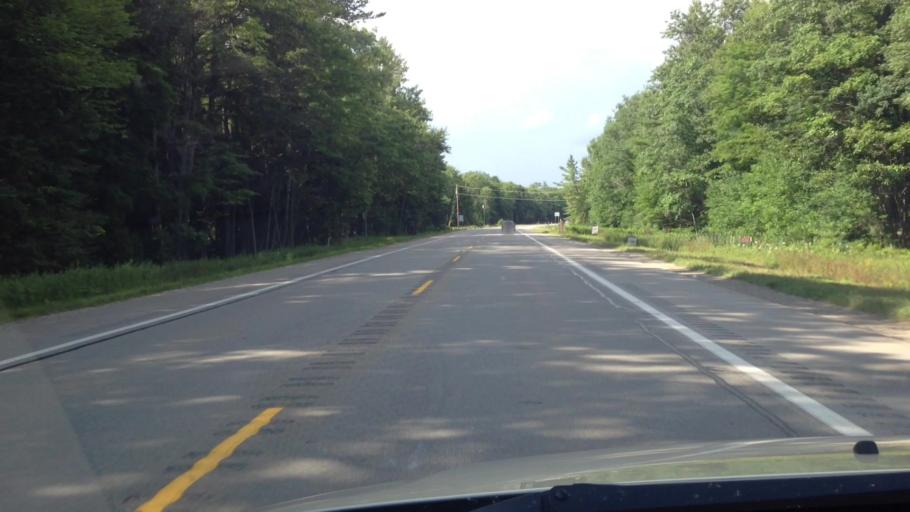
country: US
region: Michigan
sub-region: Menominee County
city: Menominee
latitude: 45.3010
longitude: -87.4394
